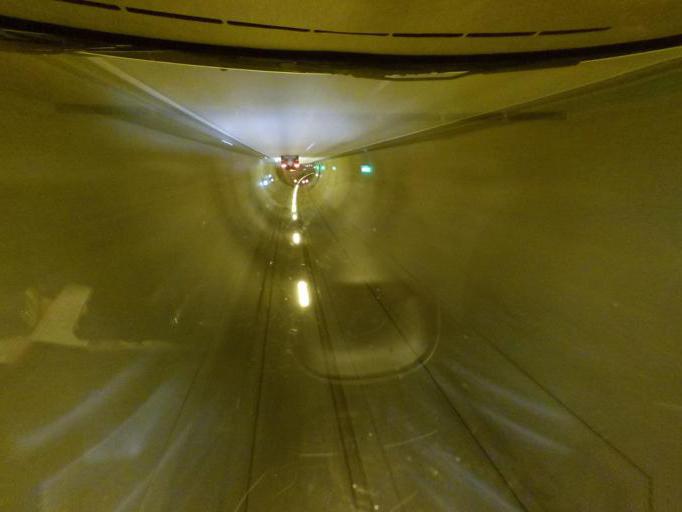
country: DE
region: Thuringia
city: Rustenfelde
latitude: 51.4045
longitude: 9.9983
